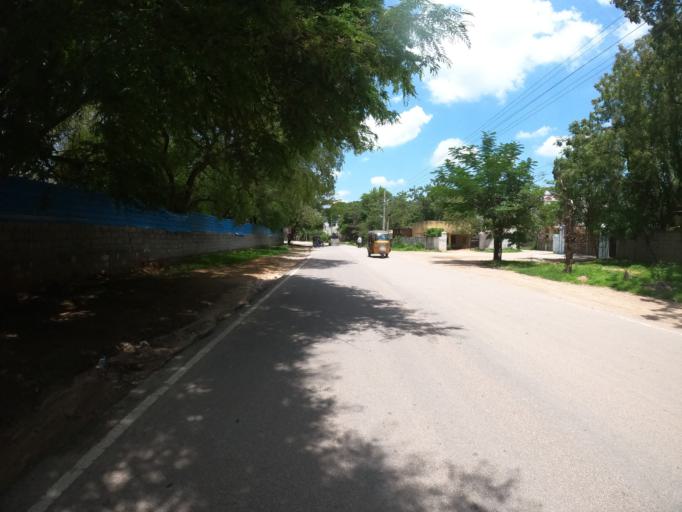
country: IN
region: Telangana
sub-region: Medak
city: Serilingampalle
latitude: 17.3853
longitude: 78.3190
